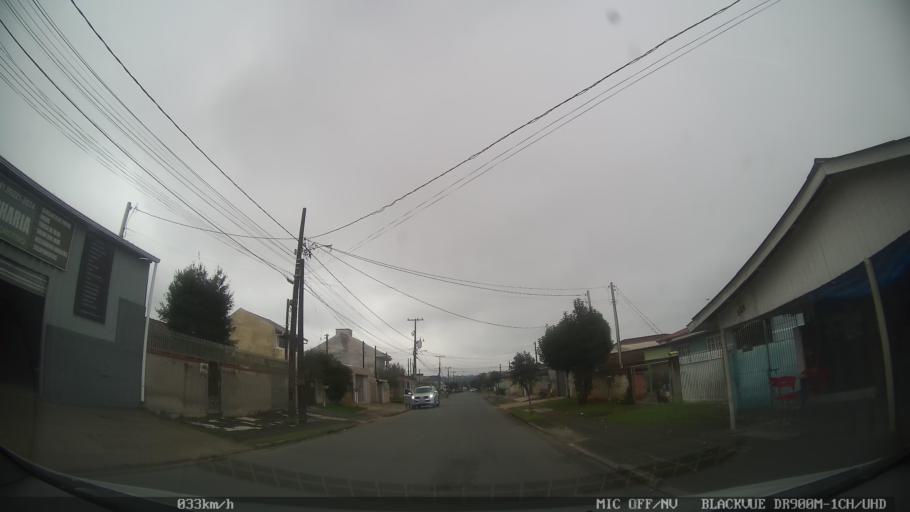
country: BR
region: Parana
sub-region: Sao Jose Dos Pinhais
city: Sao Jose dos Pinhais
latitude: -25.6089
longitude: -49.1665
